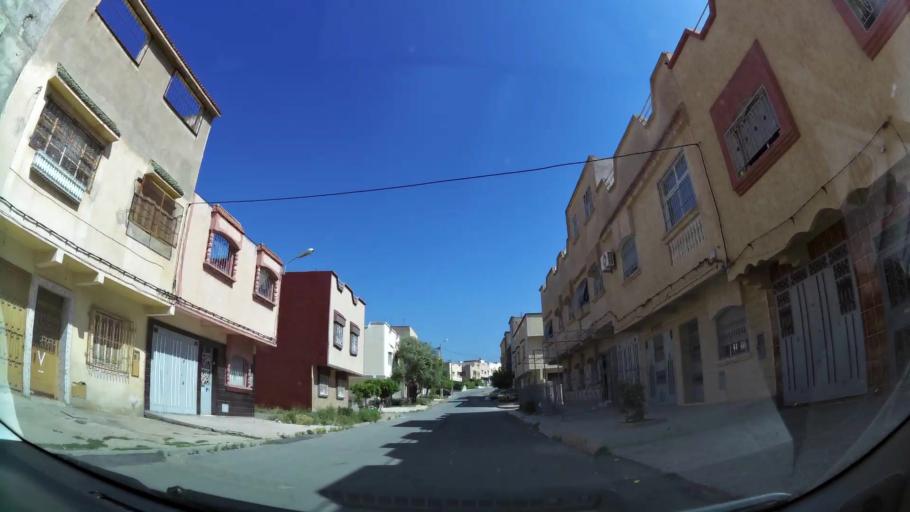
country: MA
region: Oriental
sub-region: Oujda-Angad
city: Oujda
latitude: 34.6931
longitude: -1.8772
